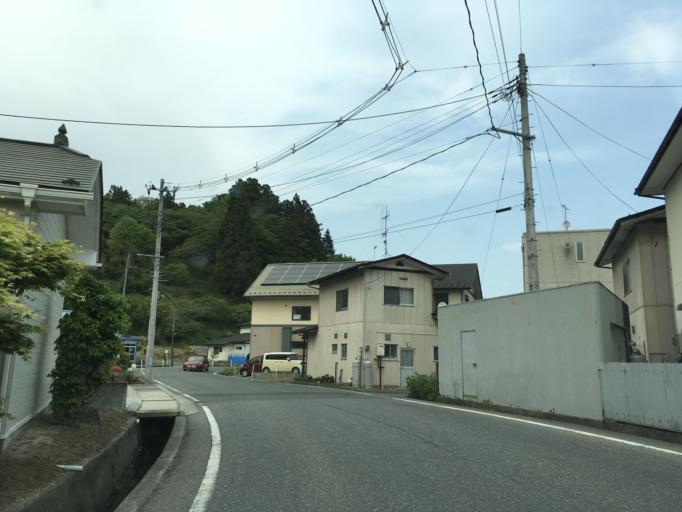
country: JP
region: Iwate
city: Ofunato
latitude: 38.8887
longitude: 141.5529
